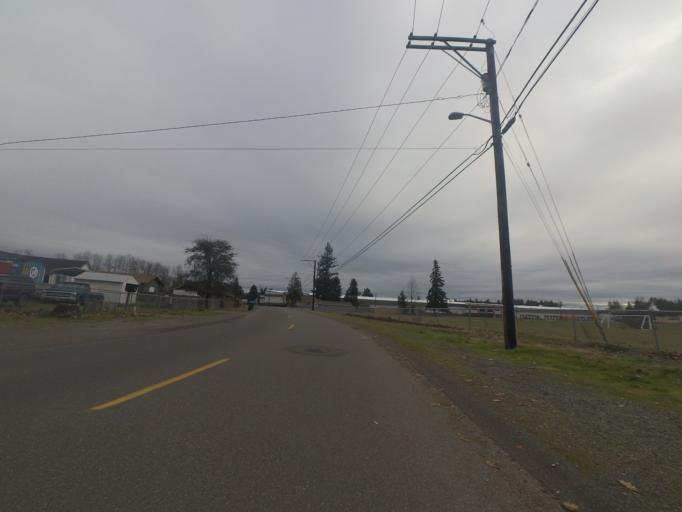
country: US
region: Washington
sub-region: Pierce County
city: Fort Lewis
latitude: 47.1246
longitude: -122.5397
